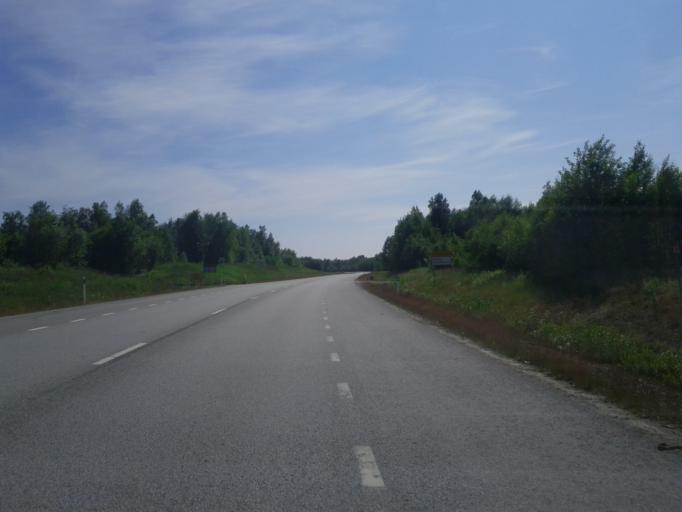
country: SE
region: Vaesterbotten
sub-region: Umea Kommun
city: Umea
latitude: 63.7797
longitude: 20.3027
